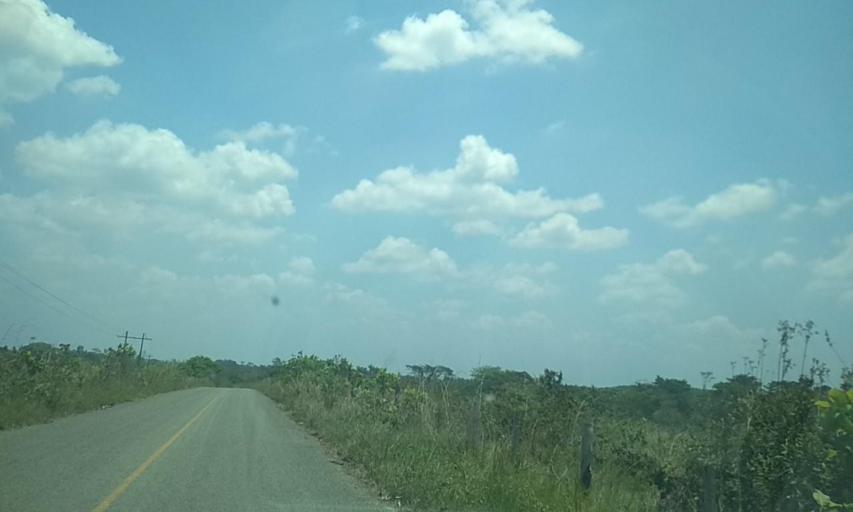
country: MX
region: Tabasco
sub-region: Huimanguillo
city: Francisco Rueda
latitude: 17.8239
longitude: -93.8718
